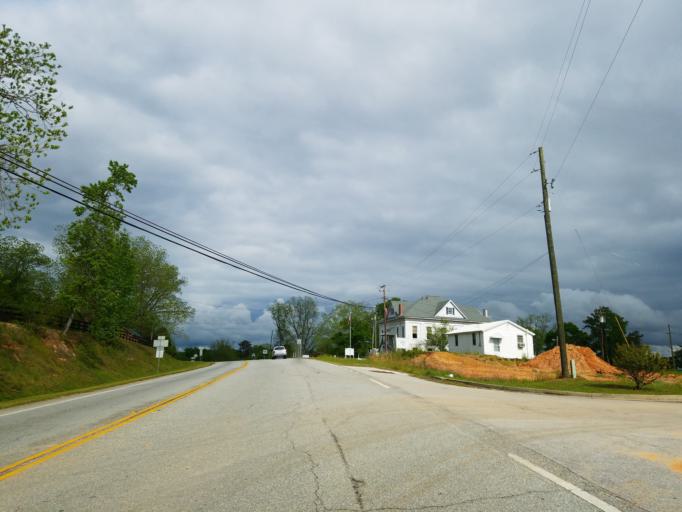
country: US
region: Georgia
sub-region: Crawford County
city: Knoxville
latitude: 32.7249
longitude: -83.9991
